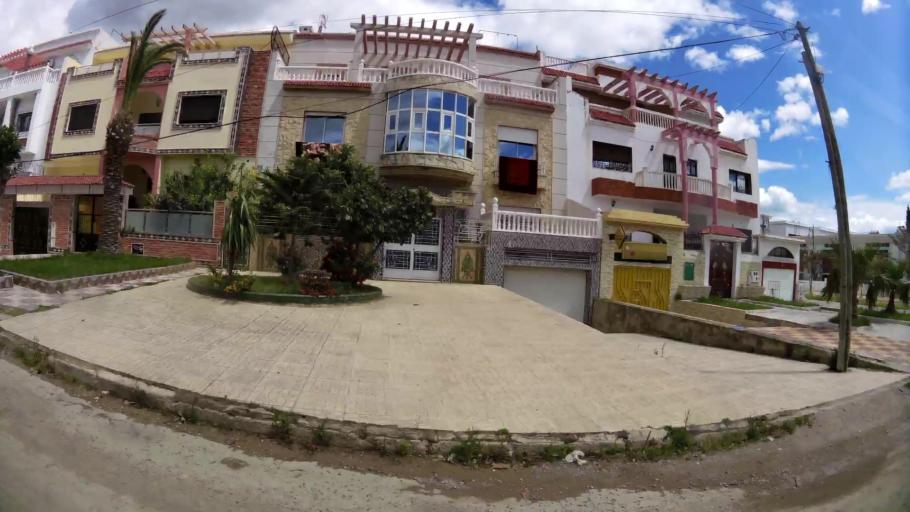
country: MA
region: Tanger-Tetouan
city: Tetouan
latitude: 35.5853
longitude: -5.3397
